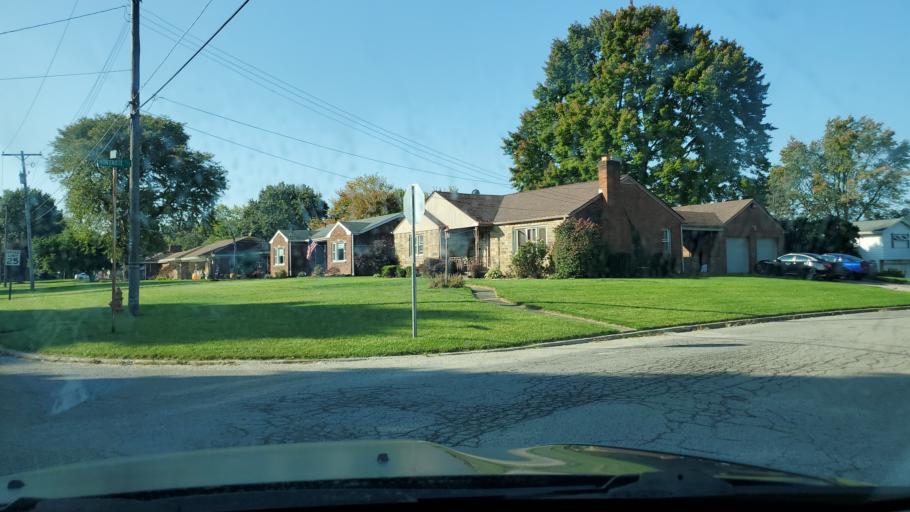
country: US
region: Ohio
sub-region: Mahoning County
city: Boardman
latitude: 41.0506
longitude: -80.6487
